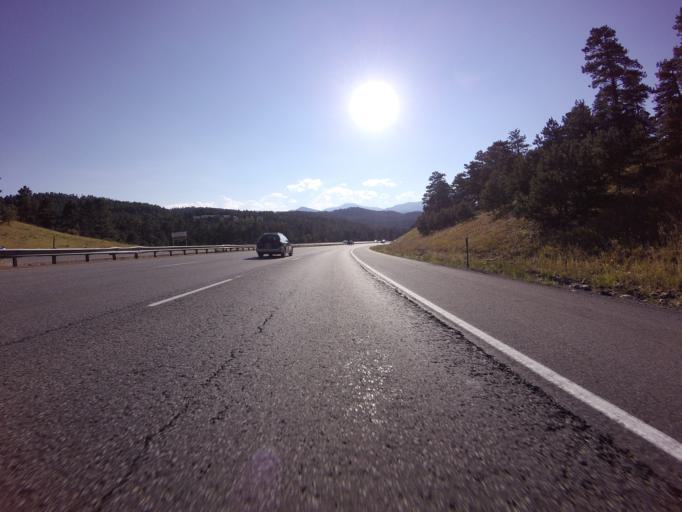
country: US
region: Colorado
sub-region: Jefferson County
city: Kittredge
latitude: 39.7017
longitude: -105.3318
